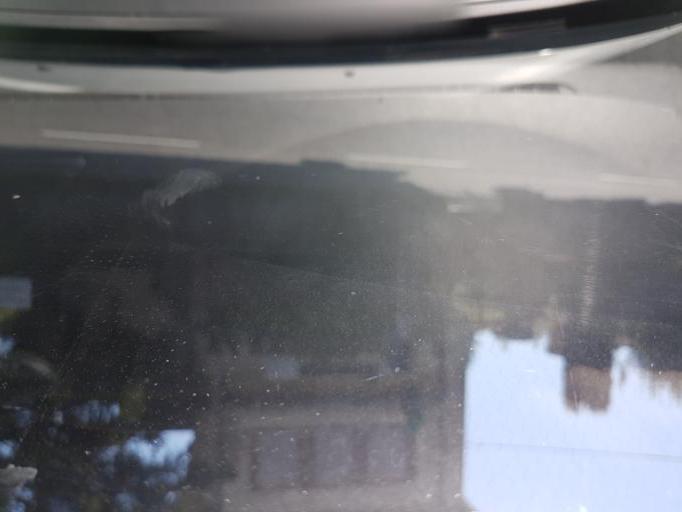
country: IT
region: Friuli Venezia Giulia
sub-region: Provincia di Trieste
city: Aurisina
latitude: 45.7498
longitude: 13.6723
